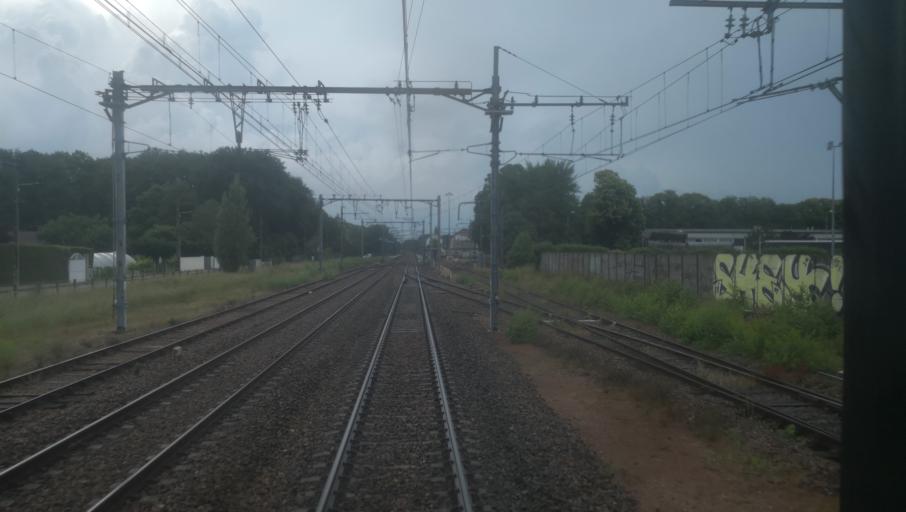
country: FR
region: Centre
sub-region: Departement du Loiret
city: Saint-Cyr-en-Val
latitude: 47.8161
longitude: 1.9470
